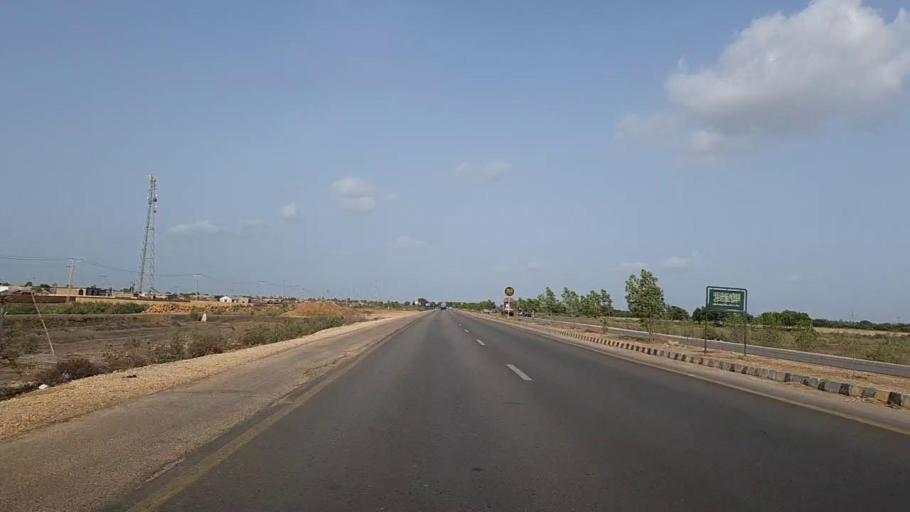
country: PK
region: Sindh
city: Gharo
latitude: 24.7397
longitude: 67.7514
